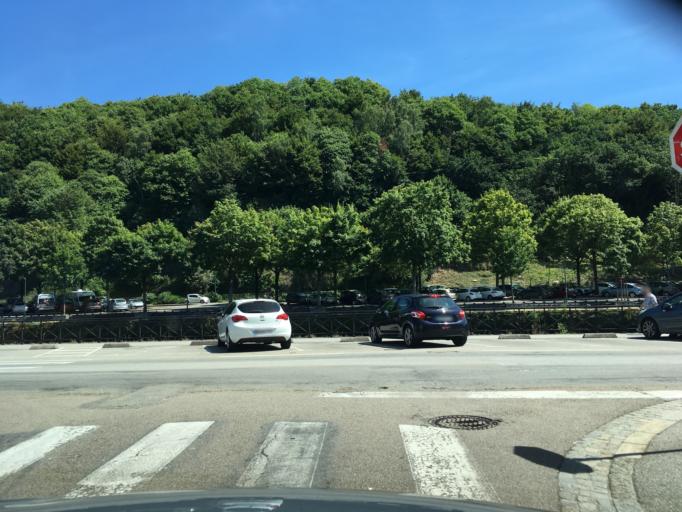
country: FR
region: Brittany
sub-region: Departement du Finistere
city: Quimper
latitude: 47.9919
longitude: -4.1101
